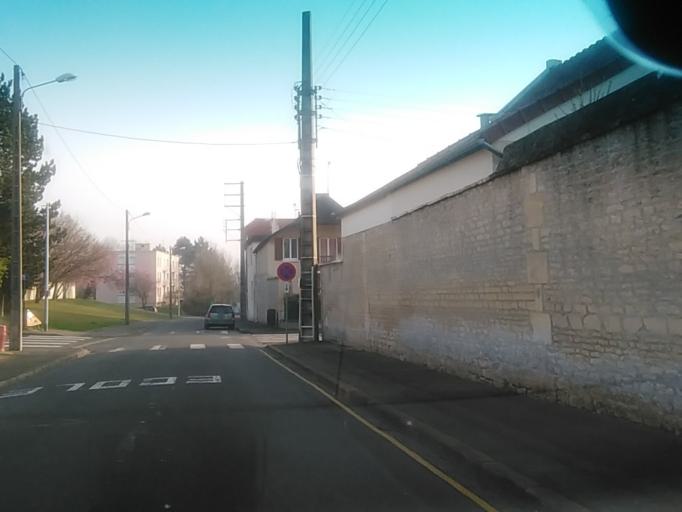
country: FR
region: Lower Normandy
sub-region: Departement du Calvados
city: Saint-Germain-la-Blanche-Herbe
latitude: 49.1779
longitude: -0.3862
